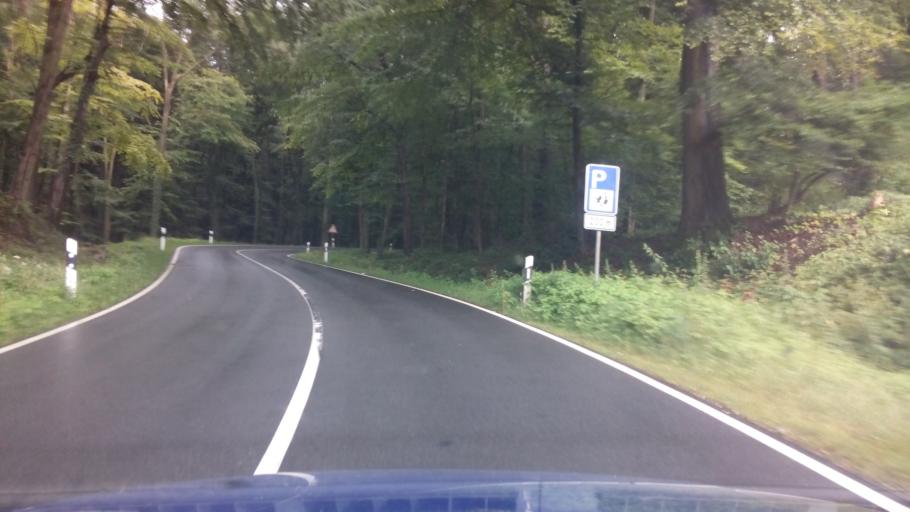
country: DE
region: Lower Saxony
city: Bad Essen
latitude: 52.3084
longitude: 8.3288
